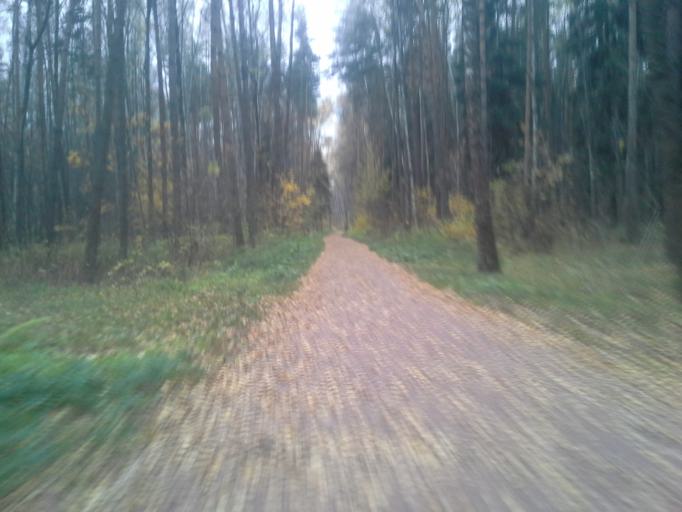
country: RU
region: Moskovskaya
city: Zarech'ye
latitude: 55.6653
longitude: 37.4017
